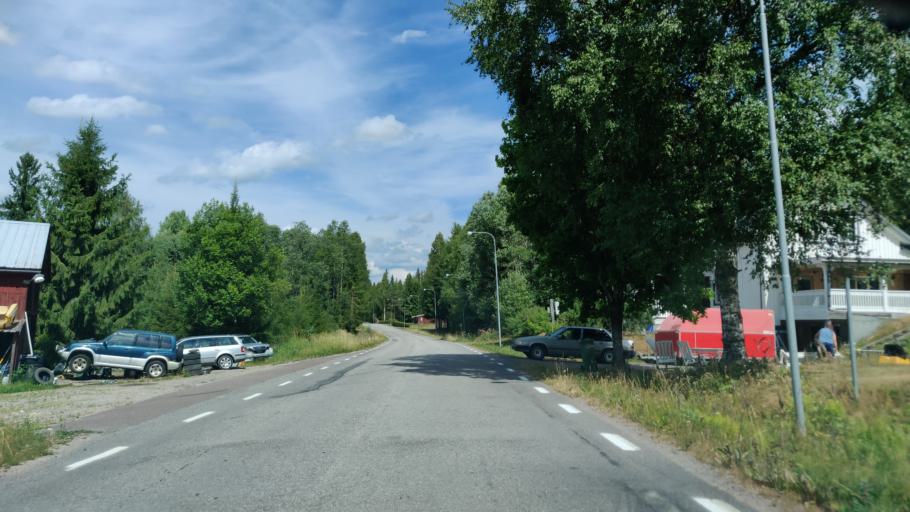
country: SE
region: Vaermland
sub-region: Hagfors Kommun
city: Ekshaerad
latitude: 60.1090
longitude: 13.5012
